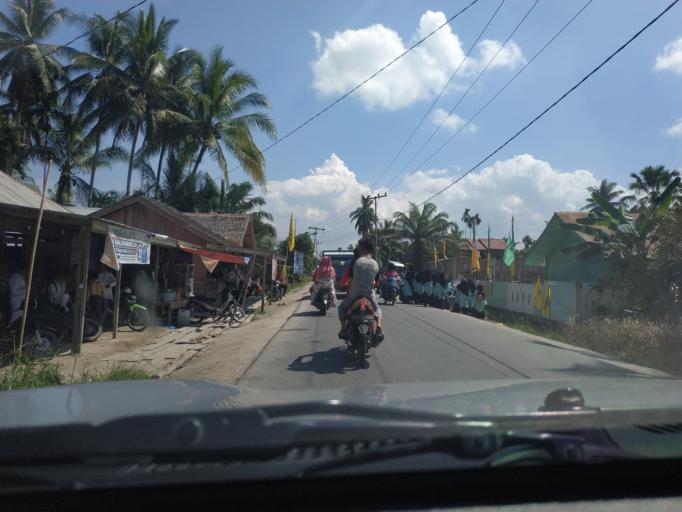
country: ID
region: North Sumatra
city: Tanjungbalai
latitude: 2.9316
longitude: 99.8601
